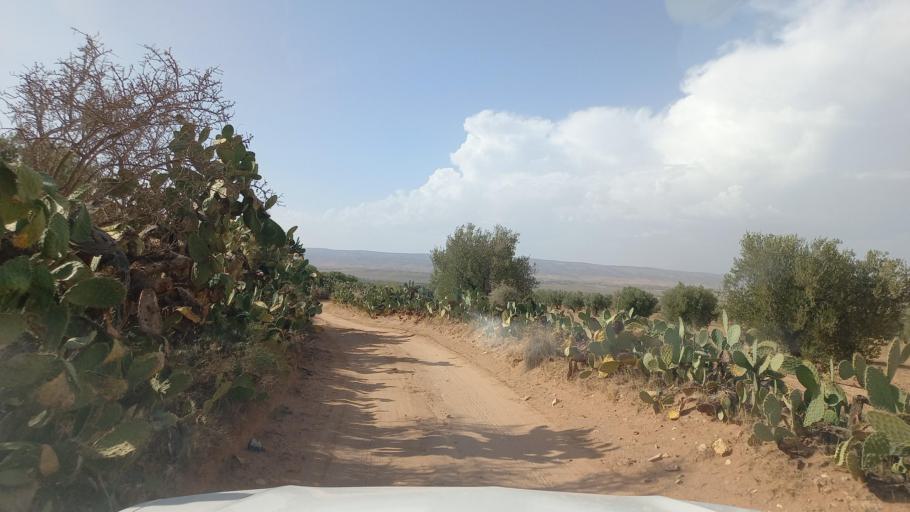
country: TN
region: Al Qasrayn
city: Kasserine
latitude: 35.2067
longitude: 8.9686
